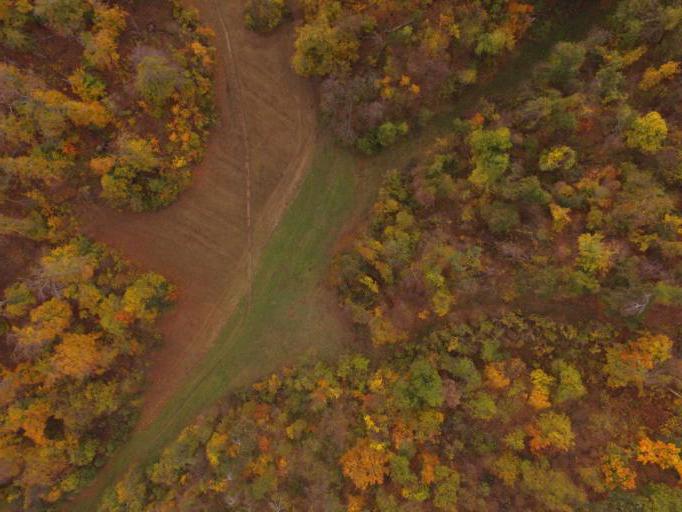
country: HU
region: Pest
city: Budakeszi
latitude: 47.5071
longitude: 18.9683
